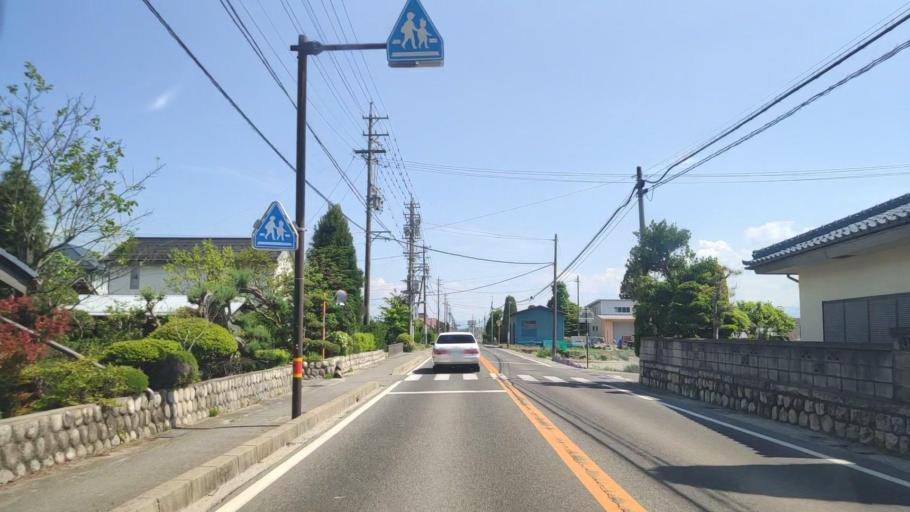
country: JP
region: Nagano
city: Hotaka
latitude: 36.3682
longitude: 137.8757
